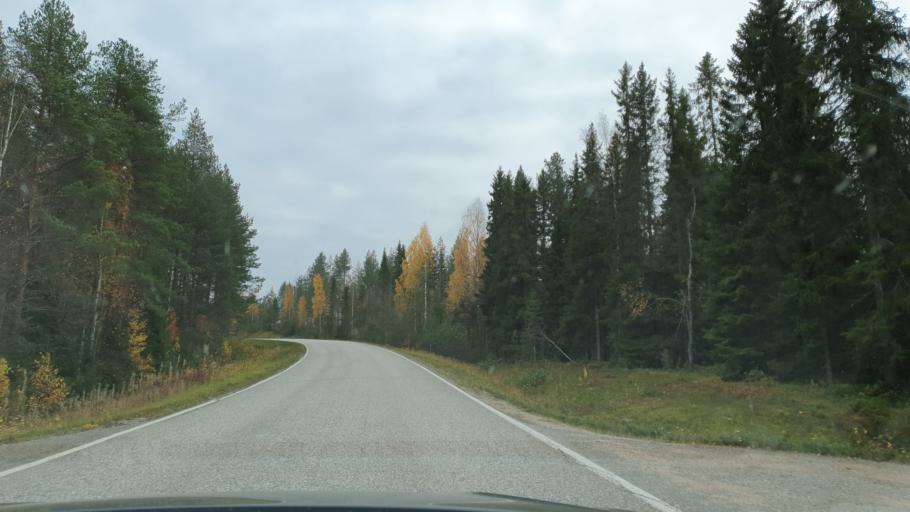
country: FI
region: Kainuu
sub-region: Kajaani
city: Ristijaervi
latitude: 64.4722
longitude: 28.2907
